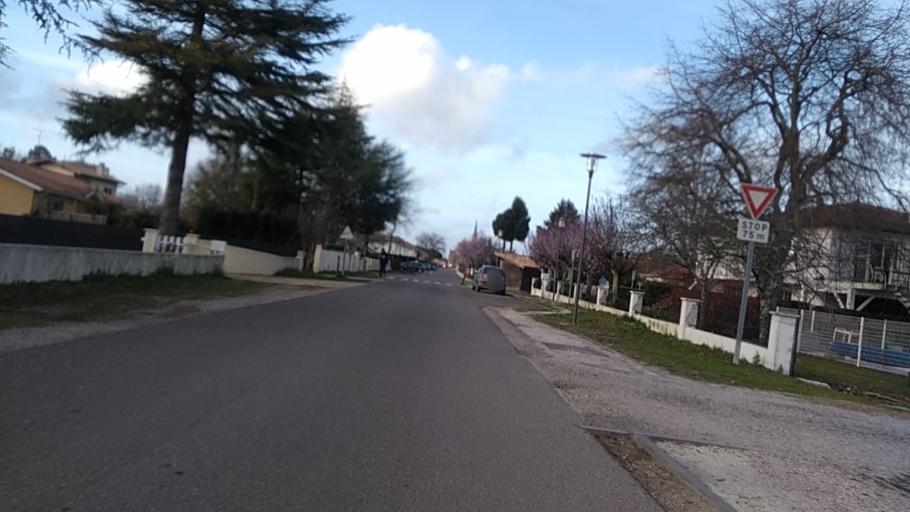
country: FR
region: Aquitaine
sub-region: Departement de la Gironde
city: Le Barp
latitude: 44.6014
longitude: -0.7688
